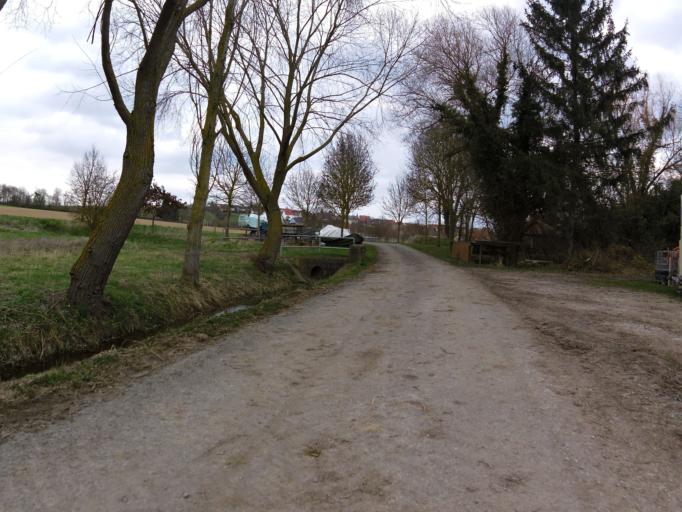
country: DE
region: Bavaria
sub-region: Regierungsbezirk Unterfranken
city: Buchbrunn
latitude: 49.7472
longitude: 10.1159
